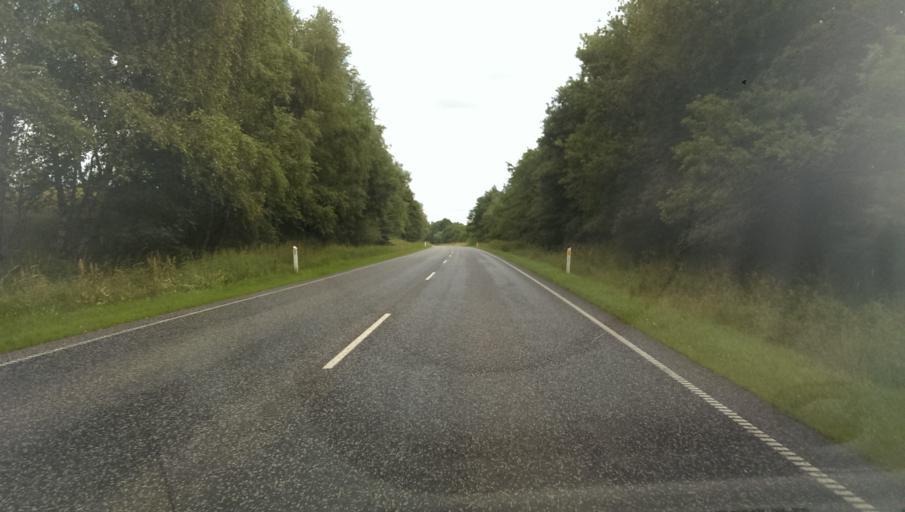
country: DK
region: South Denmark
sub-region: Vejle Kommune
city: Give
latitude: 55.9296
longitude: 9.2848
